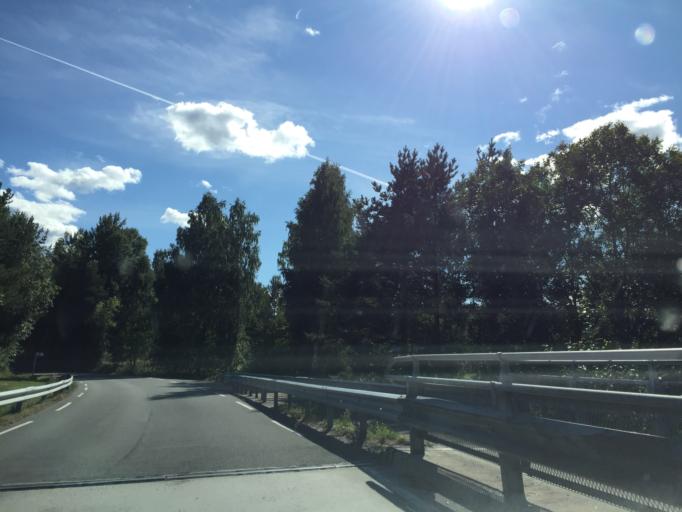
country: NO
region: Buskerud
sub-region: Ovre Eiker
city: Hokksund
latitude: 59.6998
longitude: 9.8441
